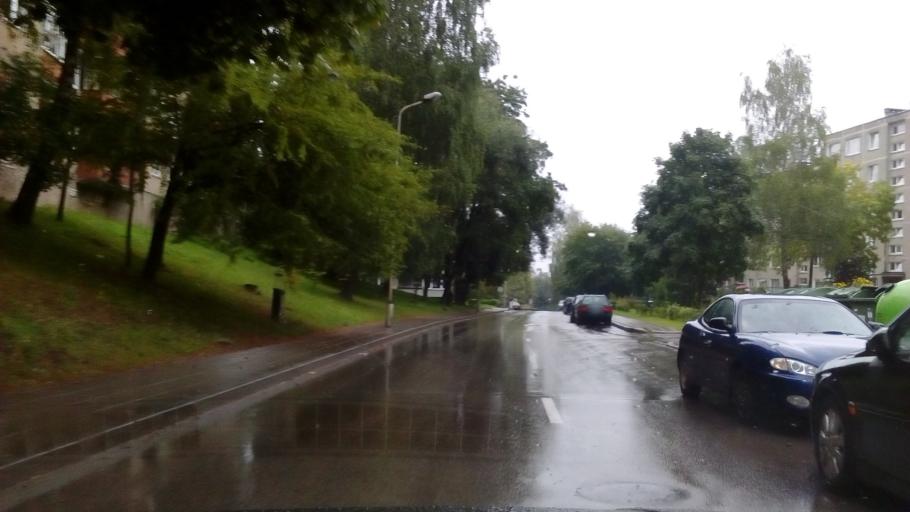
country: LT
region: Alytaus apskritis
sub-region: Alytus
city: Alytus
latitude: 54.3928
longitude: 24.0248
